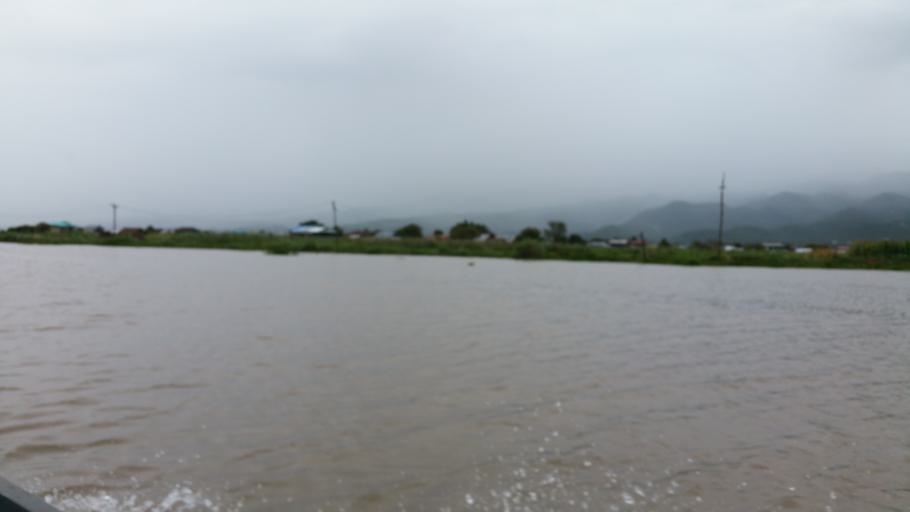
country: MM
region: Shan
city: Taunggyi
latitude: 20.6097
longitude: 96.9196
